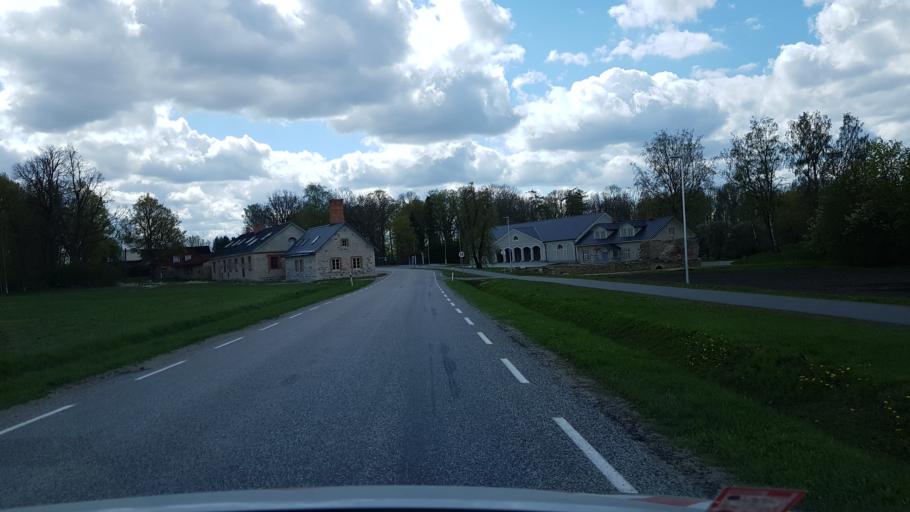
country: EE
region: Jogevamaa
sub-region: Poltsamaa linn
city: Poltsamaa
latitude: 58.7082
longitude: 25.9400
